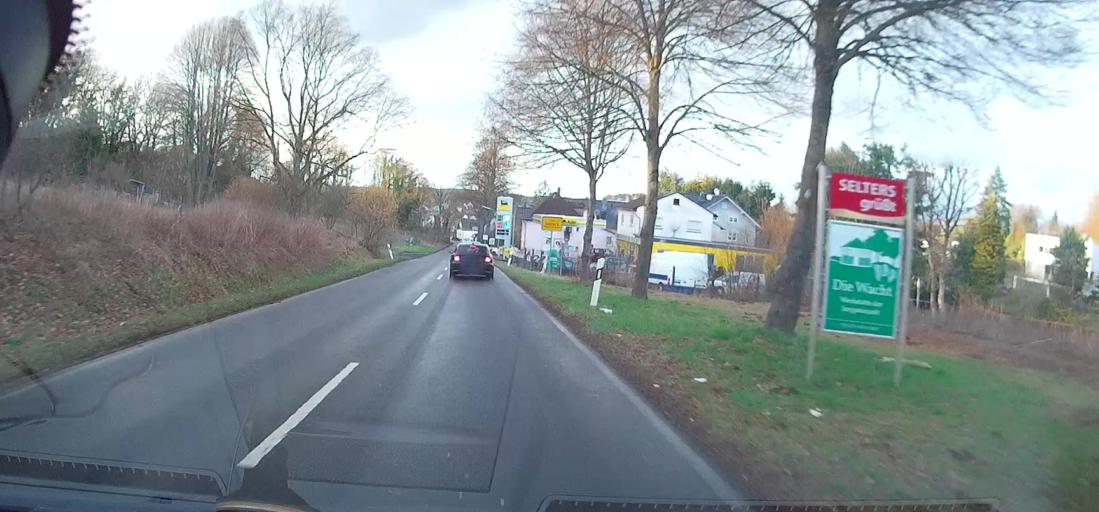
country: DE
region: Rheinland-Pfalz
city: Selters
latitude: 50.5263
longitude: 7.7599
